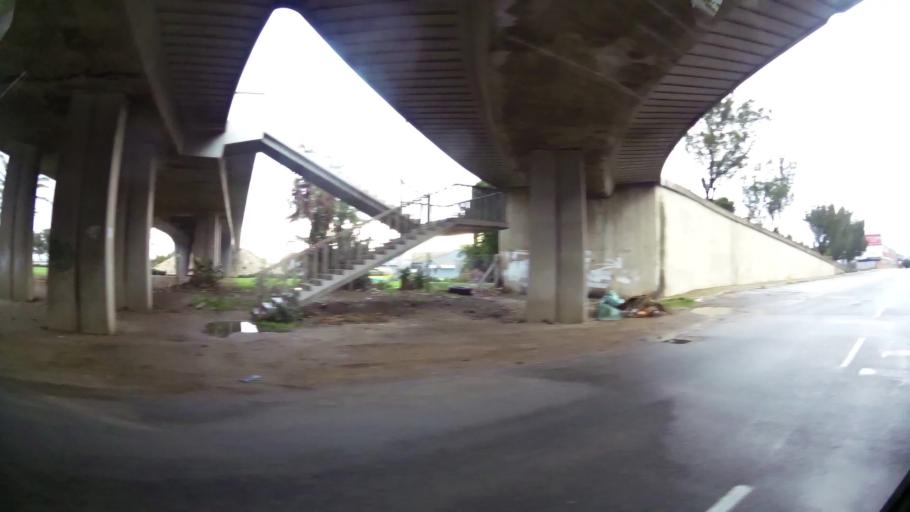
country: ZA
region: Eastern Cape
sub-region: Nelson Mandela Bay Metropolitan Municipality
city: Port Elizabeth
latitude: -33.9312
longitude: 25.6088
